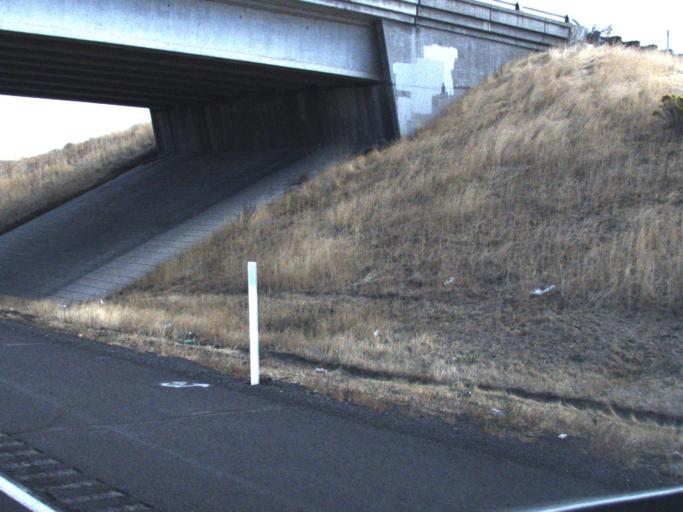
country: US
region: Washington
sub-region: Yakima County
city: Selah
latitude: 46.6238
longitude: -120.5316
